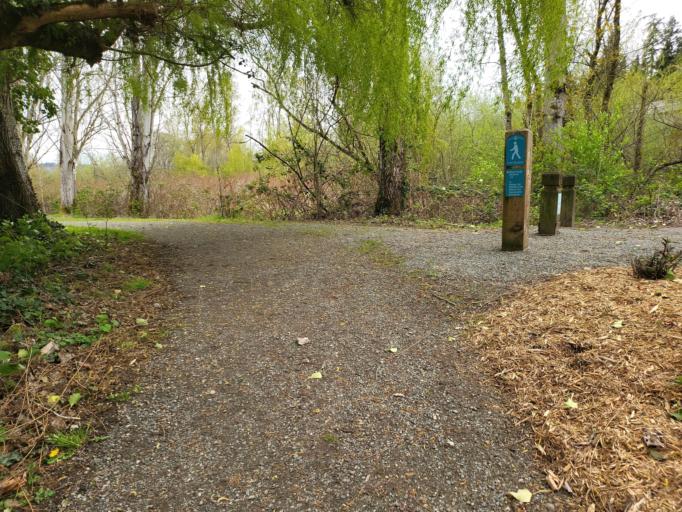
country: US
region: Washington
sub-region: King County
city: Newport
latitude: 47.5890
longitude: -122.1909
